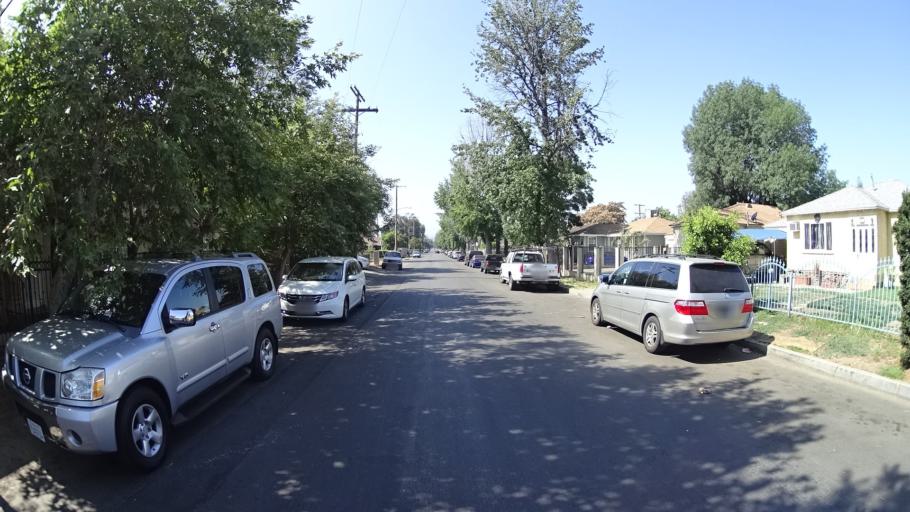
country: US
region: California
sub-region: Los Angeles County
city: Van Nuys
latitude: 34.1991
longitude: -118.4531
